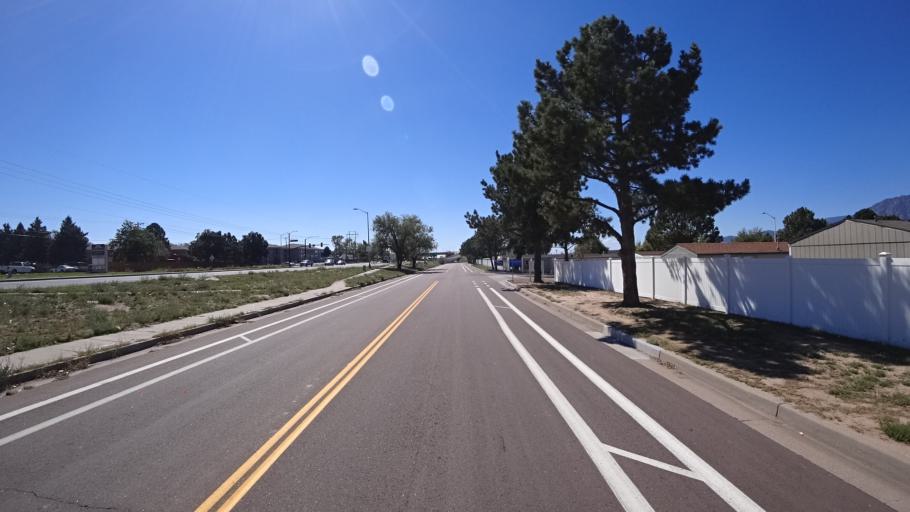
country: US
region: Colorado
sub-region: El Paso County
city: Stratmoor
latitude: 38.7853
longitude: -104.7578
